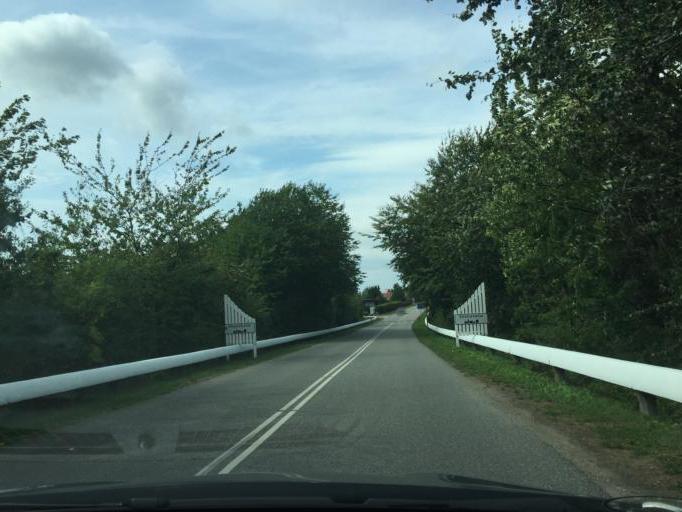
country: DK
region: South Denmark
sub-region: Assens Kommune
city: Tommerup Stationsby
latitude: 55.3889
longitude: 10.1955
